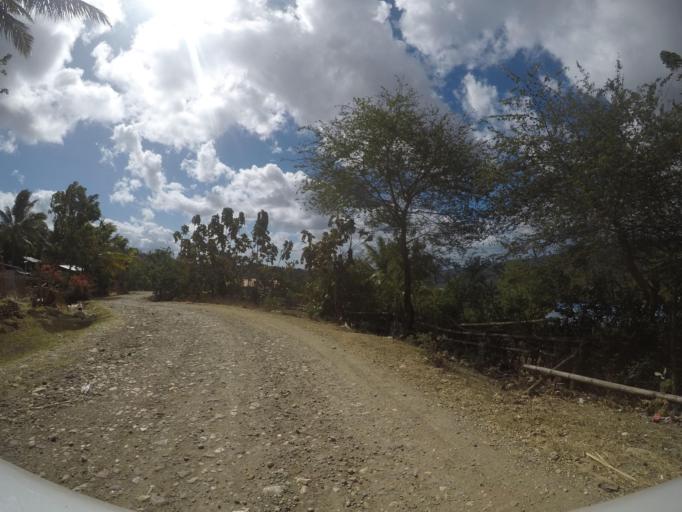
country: TL
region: Lautem
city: Lospalos
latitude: -8.5394
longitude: 126.8379
